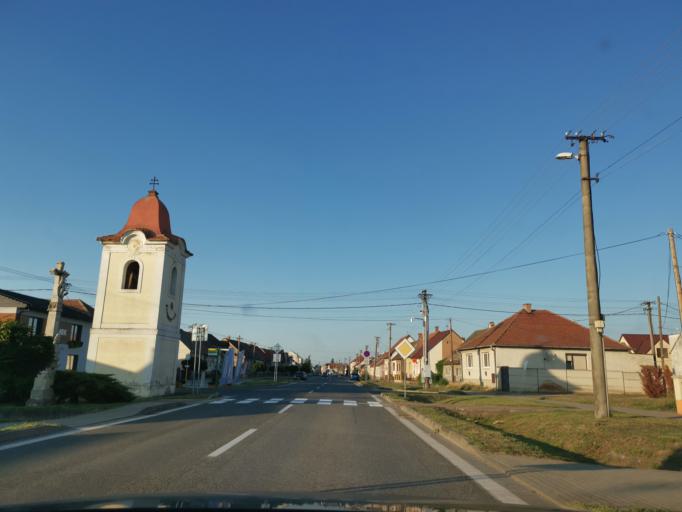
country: CZ
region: South Moravian
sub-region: Okres Breclav
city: Lanzhot
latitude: 48.6550
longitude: 17.0159
